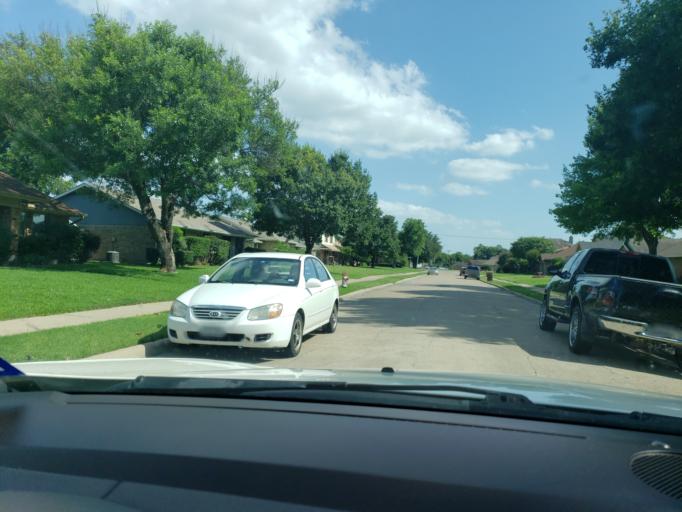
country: US
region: Texas
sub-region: Dallas County
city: Rowlett
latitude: 32.8957
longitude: -96.5761
